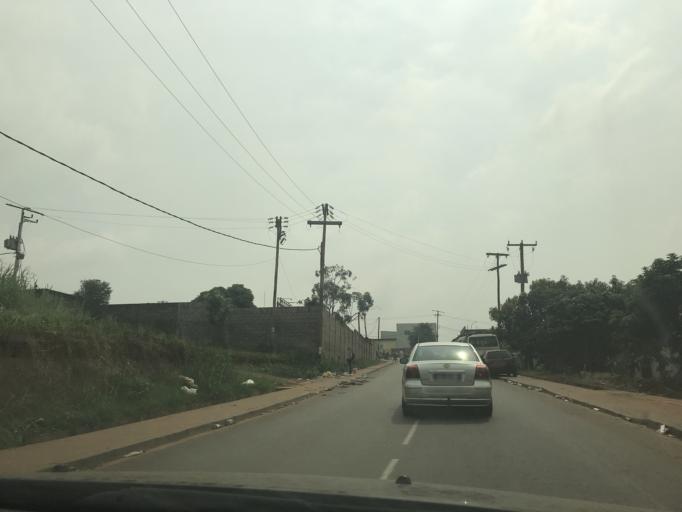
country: CM
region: Centre
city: Yaounde
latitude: 3.8217
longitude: 11.5140
